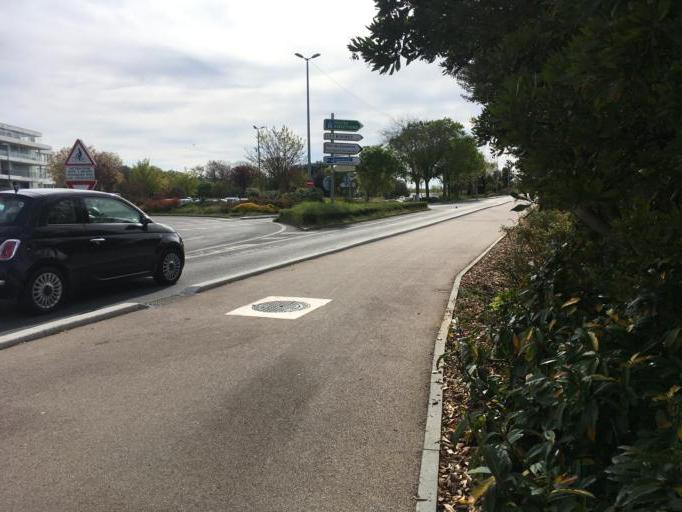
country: FR
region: Poitou-Charentes
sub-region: Departement de la Charente-Maritime
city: La Rochelle
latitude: 46.1581
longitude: -1.1454
